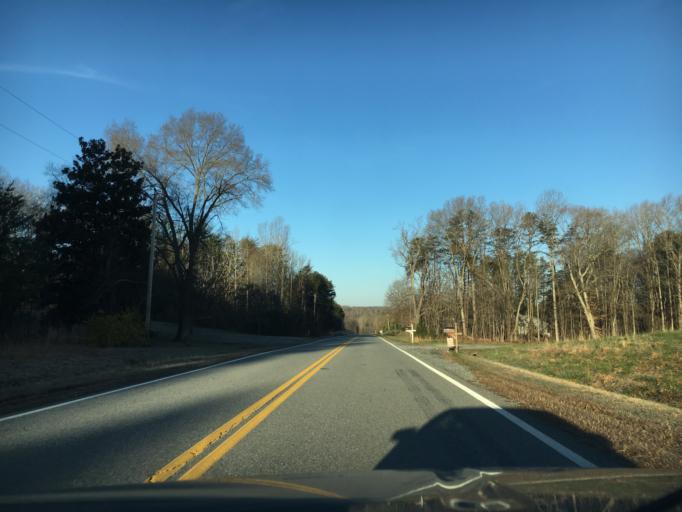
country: US
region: Virginia
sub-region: Halifax County
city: Halifax
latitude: 36.7618
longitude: -78.8961
